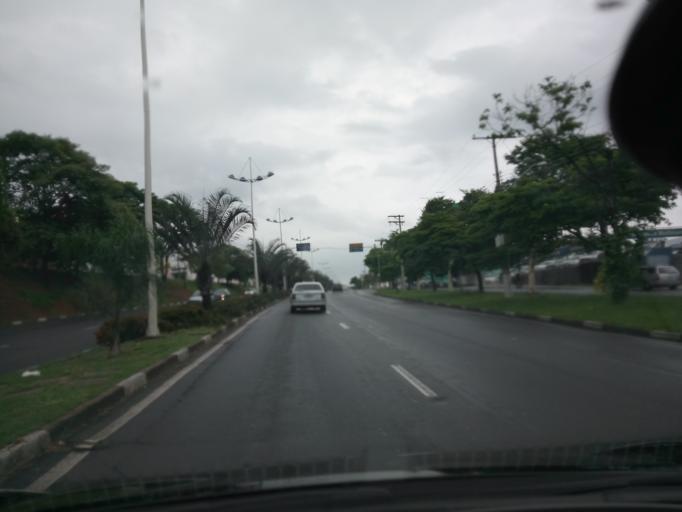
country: BR
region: Sao Paulo
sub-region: Campinas
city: Campinas
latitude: -22.9264
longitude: -47.0679
